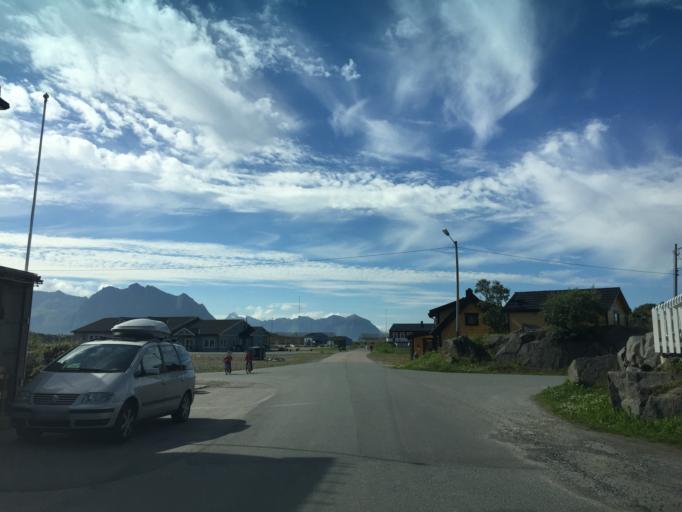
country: NO
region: Nordland
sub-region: Vagan
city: Kabelvag
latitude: 68.3883
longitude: 14.4182
